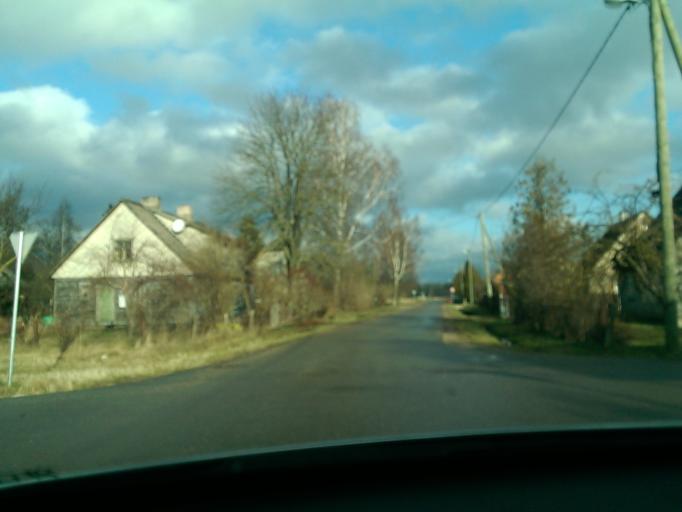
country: LV
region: Kuldigas Rajons
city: Kuldiga
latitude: 56.9755
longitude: 21.9823
